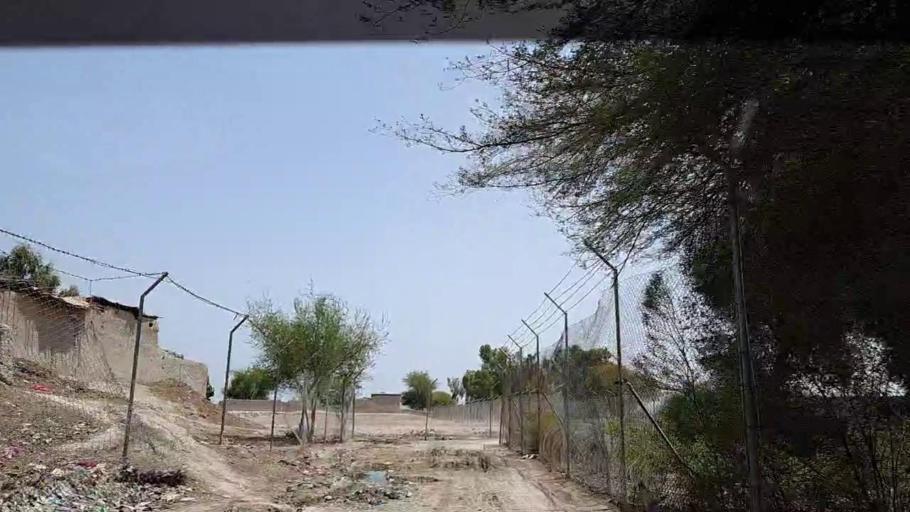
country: PK
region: Sindh
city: Johi
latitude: 26.7071
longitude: 67.6688
